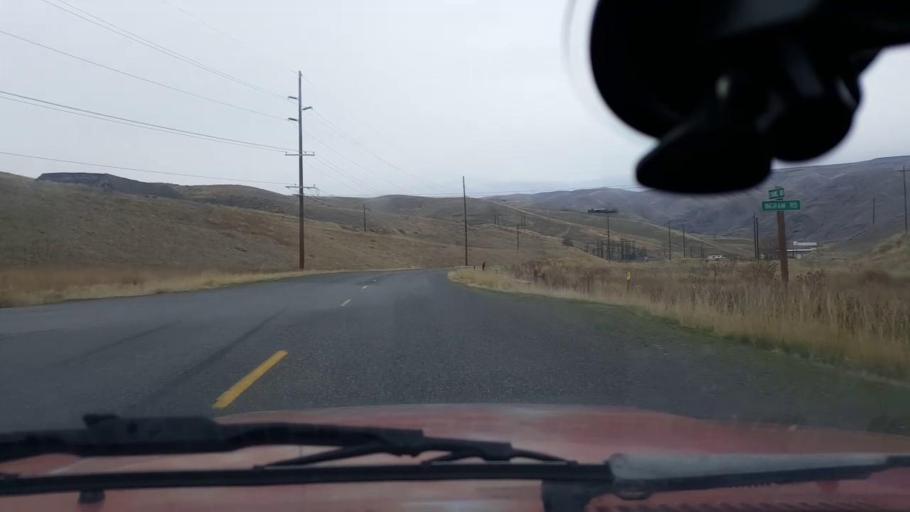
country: US
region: Washington
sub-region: Asotin County
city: Clarkston Heights-Vineland
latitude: 46.4084
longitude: -117.1085
